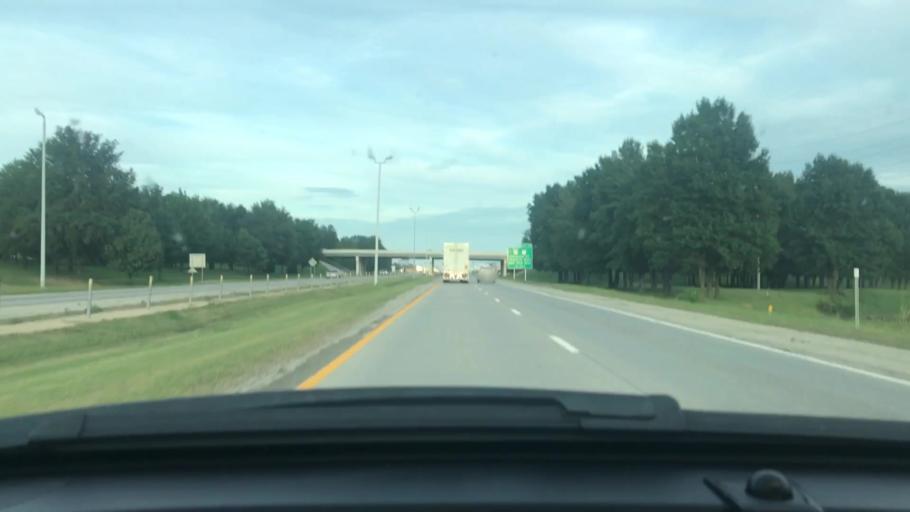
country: US
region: Arkansas
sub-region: Craighead County
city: Jonesboro
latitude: 35.8072
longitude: -90.7017
